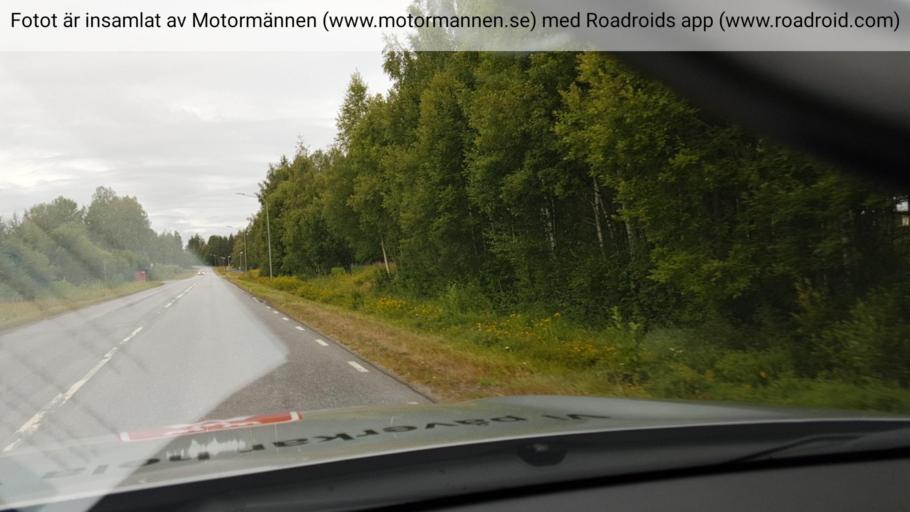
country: SE
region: Norrbotten
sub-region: Bodens Kommun
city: Boden
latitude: 65.8142
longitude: 21.6253
